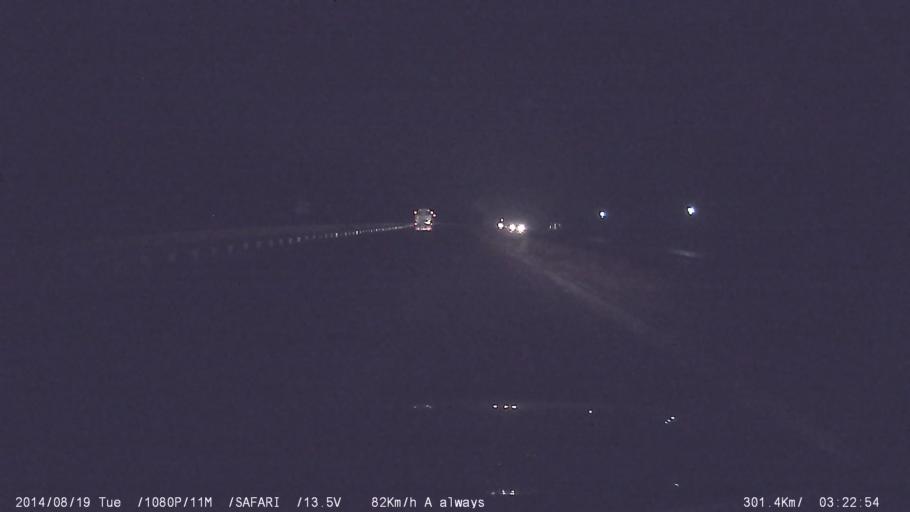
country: IN
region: Tamil Nadu
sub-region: Tiruppur
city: Avinashi
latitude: 11.1613
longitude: 77.2243
